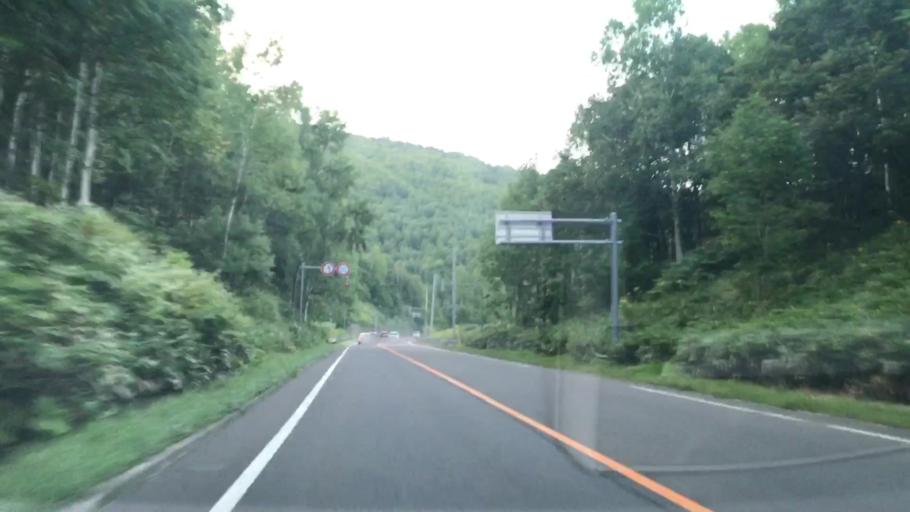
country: JP
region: Hokkaido
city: Sapporo
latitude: 42.9076
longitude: 141.1212
